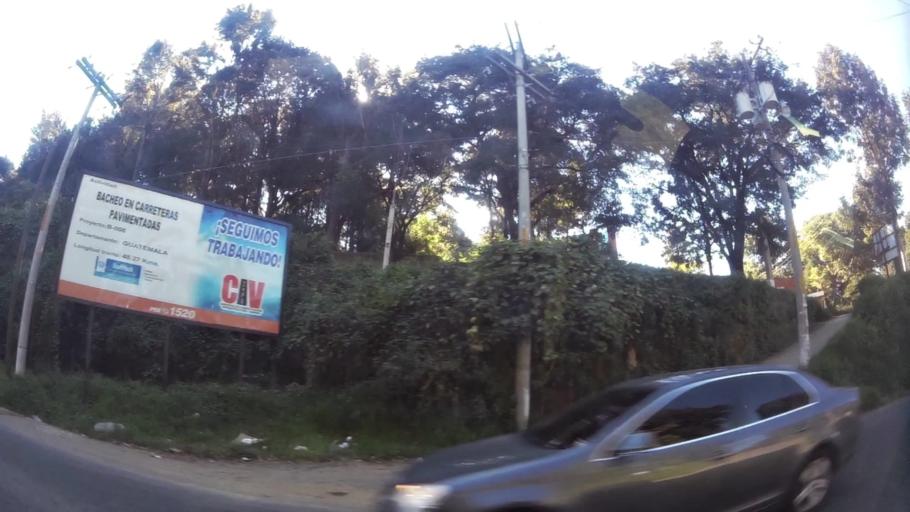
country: GT
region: Sacatepequez
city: Magdalena Milpas Altas
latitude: 14.5631
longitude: -90.6391
